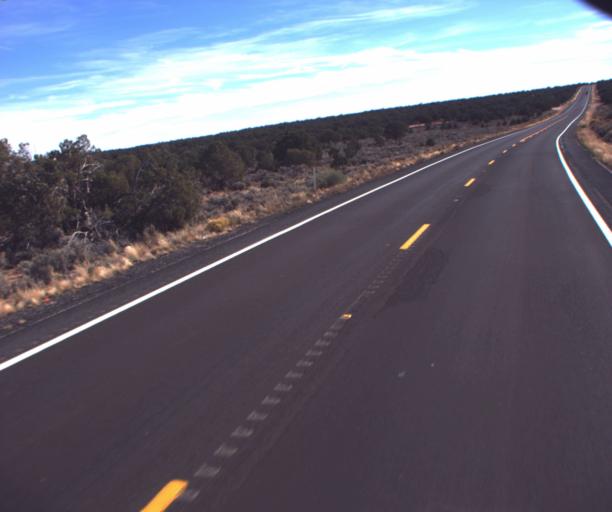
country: US
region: Arizona
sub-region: Coconino County
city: Kaibito
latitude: 36.5908
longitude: -110.8862
